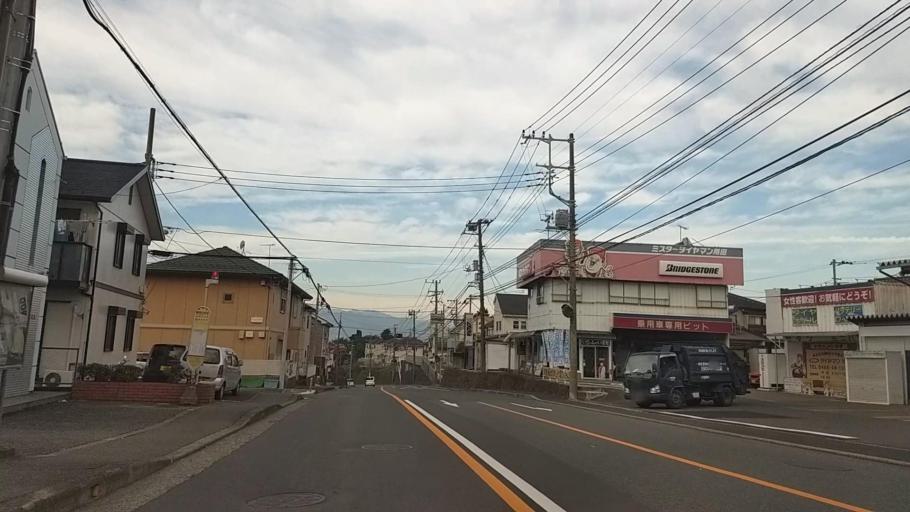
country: JP
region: Kanagawa
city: Atsugi
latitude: 35.4030
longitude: 139.4210
